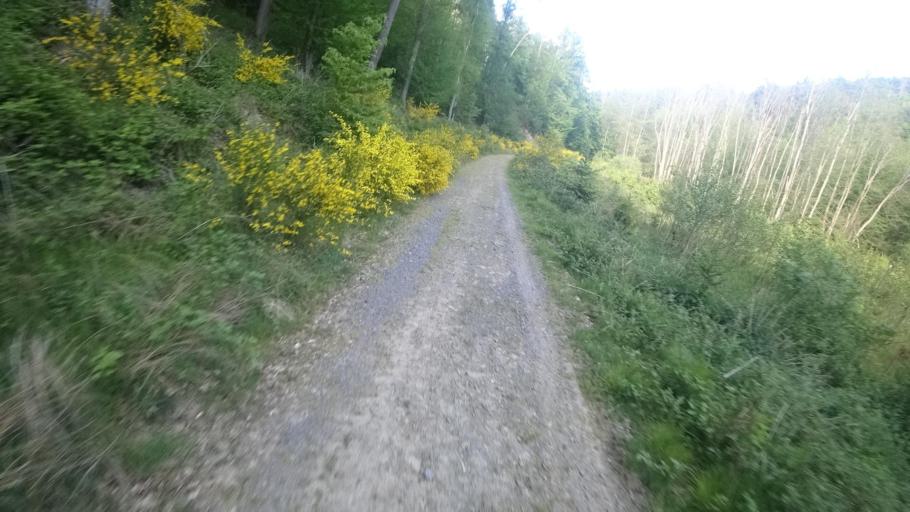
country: DE
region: Rheinland-Pfalz
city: Berg
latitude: 50.5286
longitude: 6.9672
